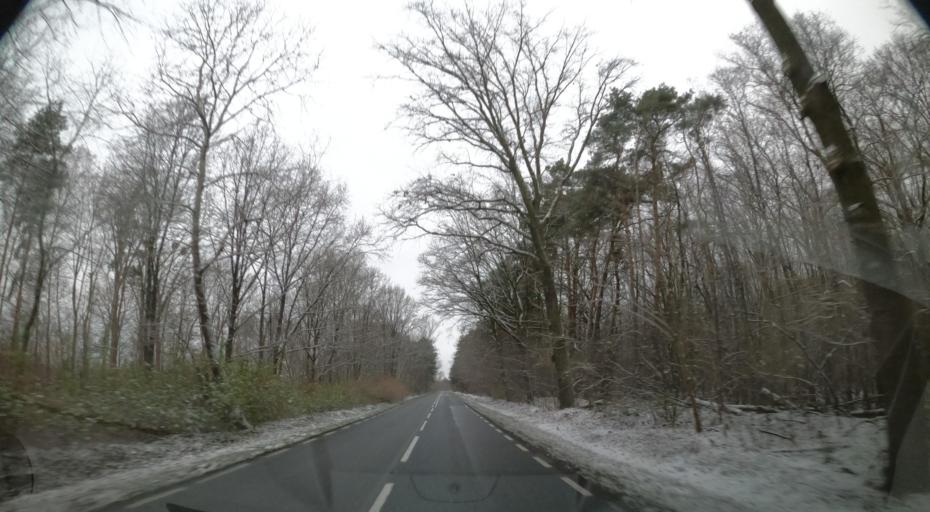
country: PL
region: Masovian Voivodeship
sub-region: Powiat plocki
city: Maszewo Duze
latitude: 52.5741
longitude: 19.5565
